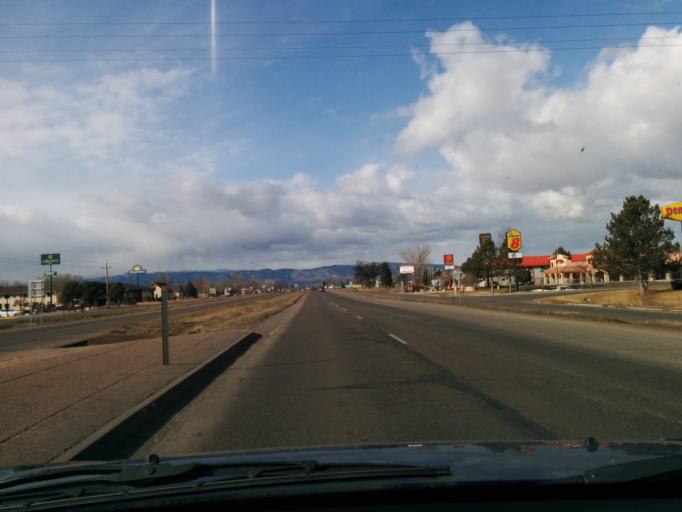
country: US
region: Colorado
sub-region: Larimer County
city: Fort Collins
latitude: 40.5812
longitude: -105.0065
